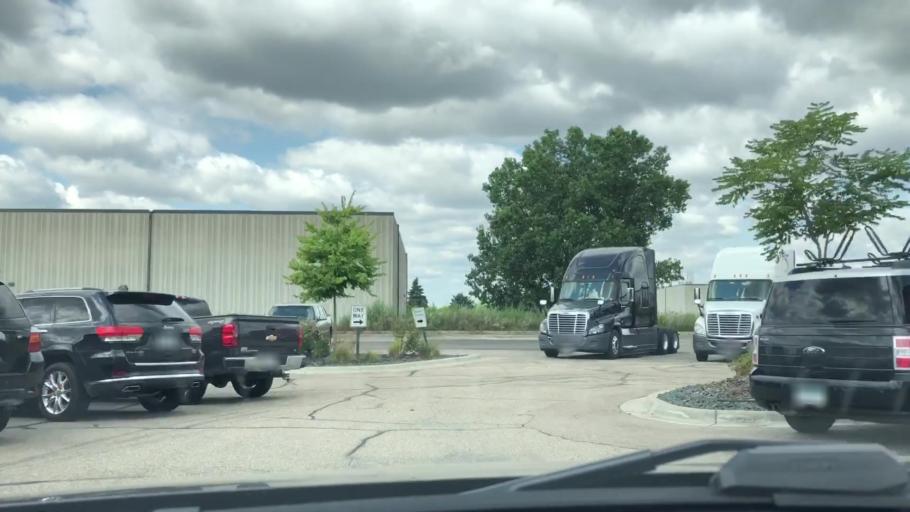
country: US
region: Minnesota
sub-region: Dakota County
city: Mendota Heights
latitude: 44.8516
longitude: -93.1532
